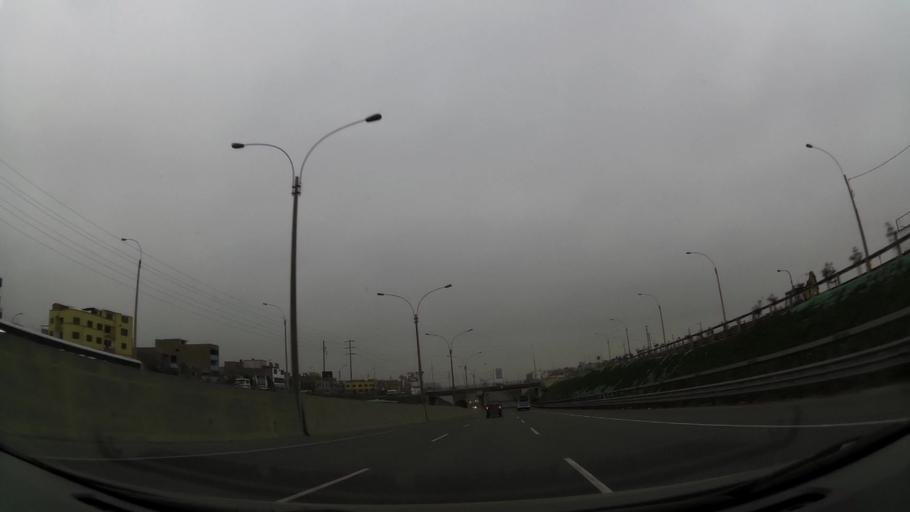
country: PE
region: Lima
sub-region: Lima
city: Independencia
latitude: -11.9439
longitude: -77.0712
